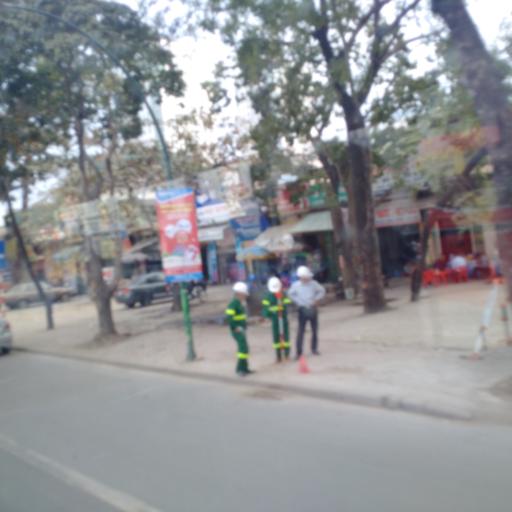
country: VN
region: Ha Noi
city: Cau Dien
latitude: 21.0469
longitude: 105.7814
